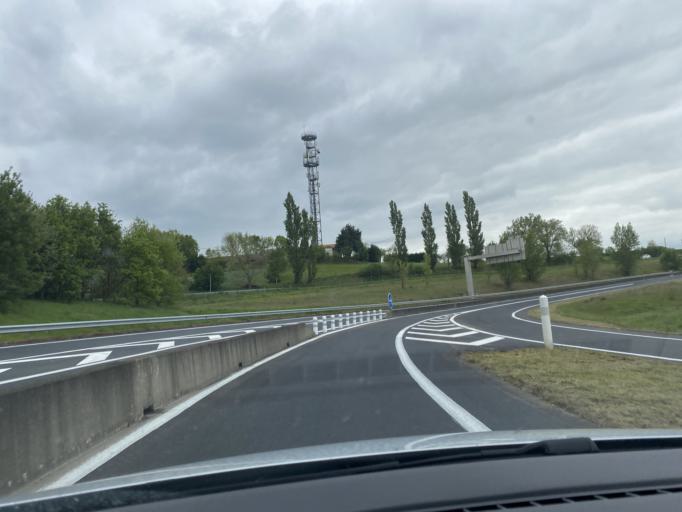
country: FR
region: Midi-Pyrenees
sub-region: Departement de la Haute-Garonne
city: Nailloux
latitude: 43.3843
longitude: 1.6225
